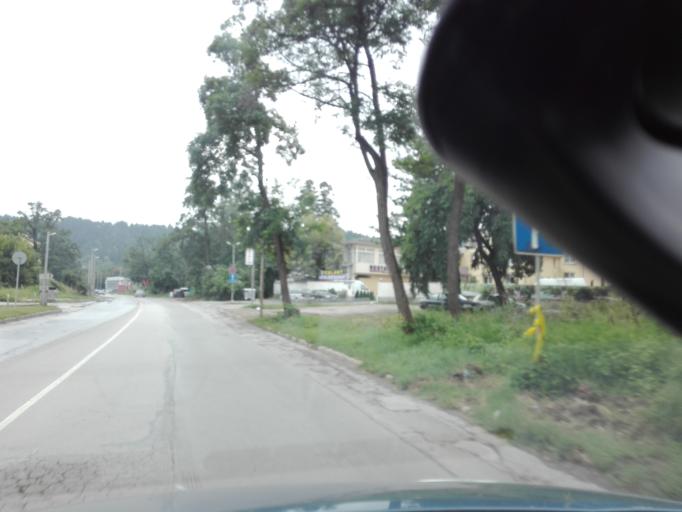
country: BG
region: Sofia-Capital
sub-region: Stolichna Obshtina
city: Sofia
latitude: 42.6122
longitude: 23.3995
